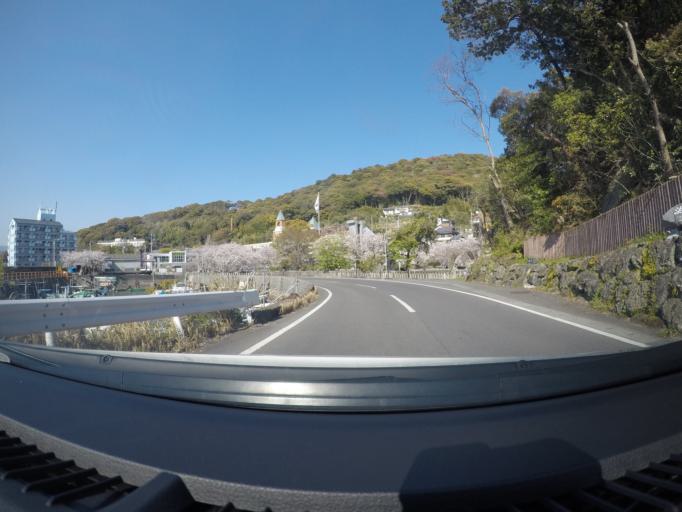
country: JP
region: Kochi
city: Kochi-shi
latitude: 33.5451
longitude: 133.5700
